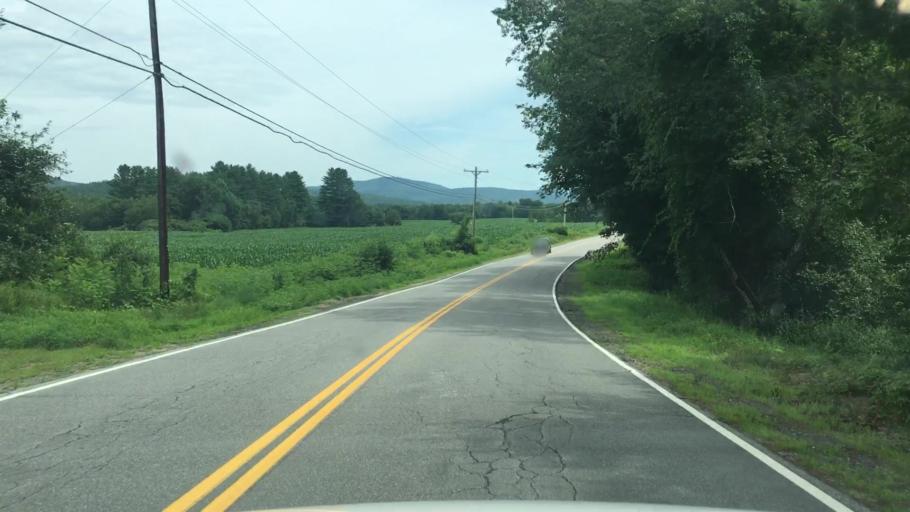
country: US
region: New Hampshire
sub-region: Grafton County
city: Plymouth
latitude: 43.7784
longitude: -71.7473
